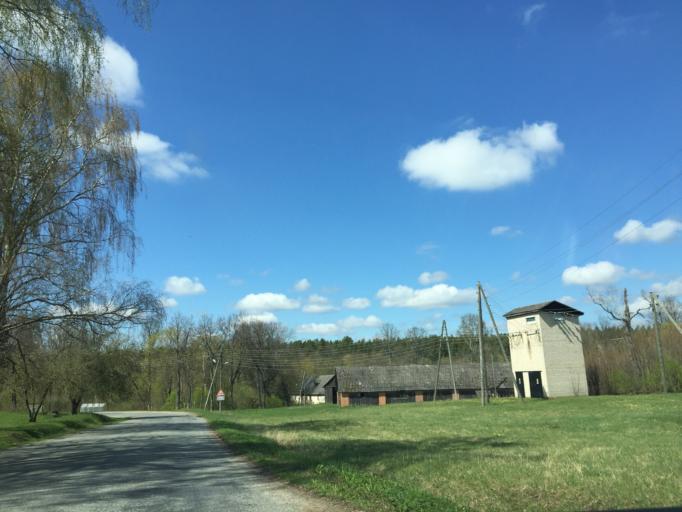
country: LV
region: Smiltene
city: Smiltene
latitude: 57.5862
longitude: 25.9568
